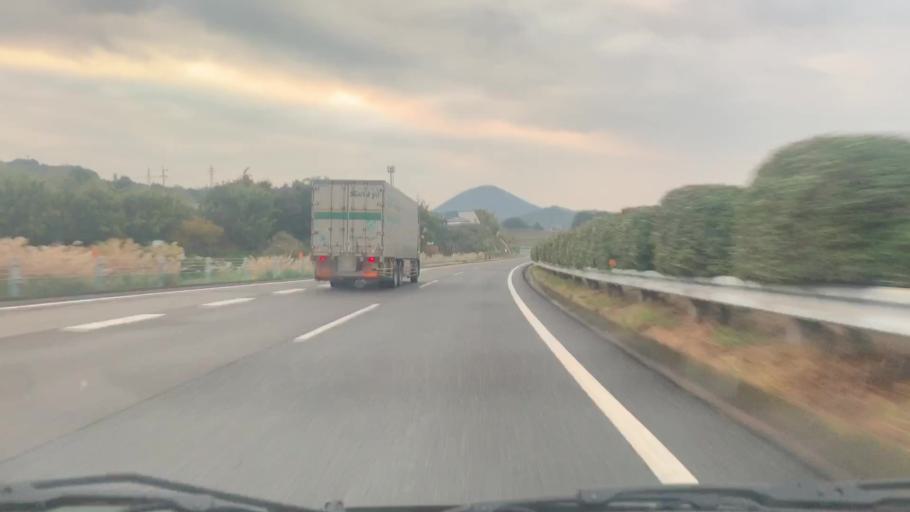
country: JP
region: Nagasaki
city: Omura
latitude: 33.0150
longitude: 129.9499
